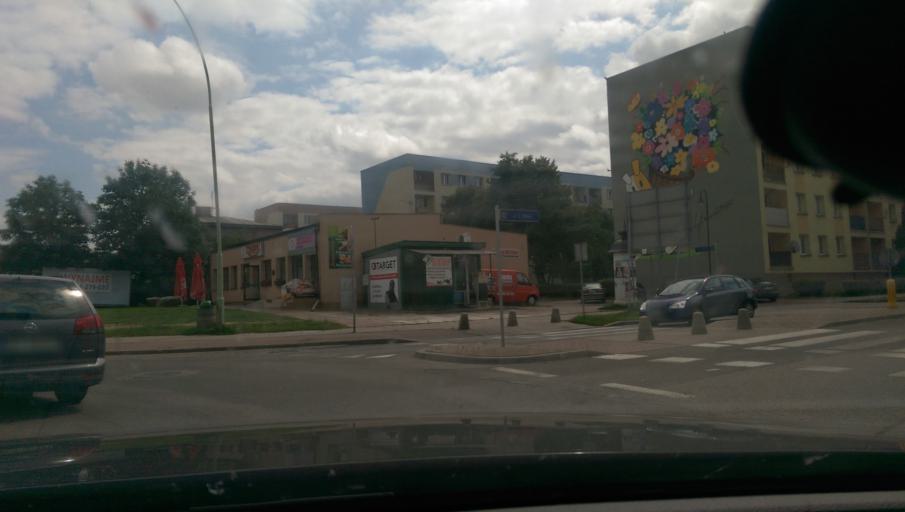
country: PL
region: Podlasie
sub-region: Suwalki
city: Suwalki
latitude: 54.1063
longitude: 22.9245
